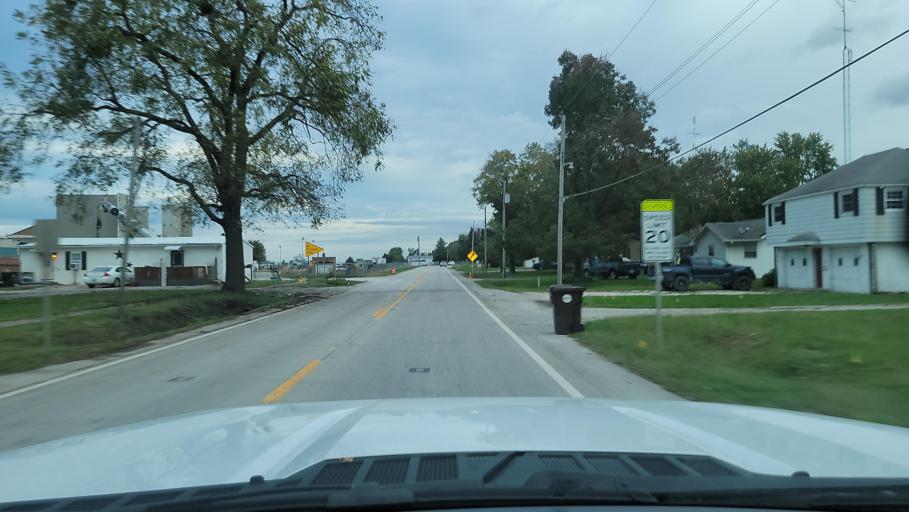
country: US
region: Illinois
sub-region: Schuyler County
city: Rushville
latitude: 40.1264
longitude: -90.5636
